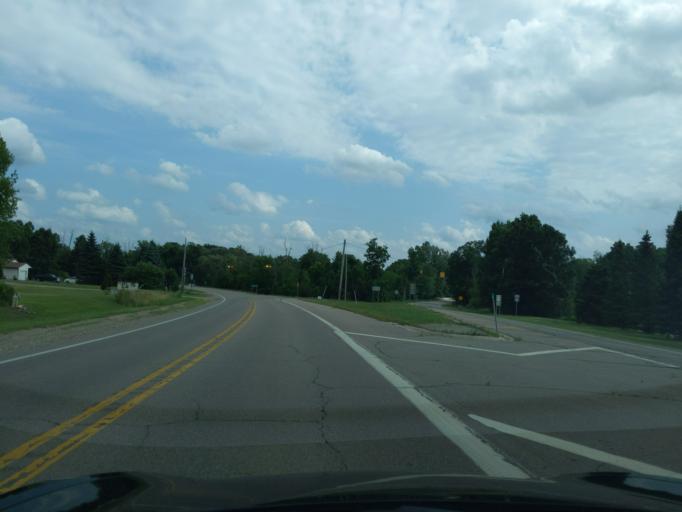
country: US
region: Michigan
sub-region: Eaton County
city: Eaton Rapids
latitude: 42.4236
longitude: -84.6496
